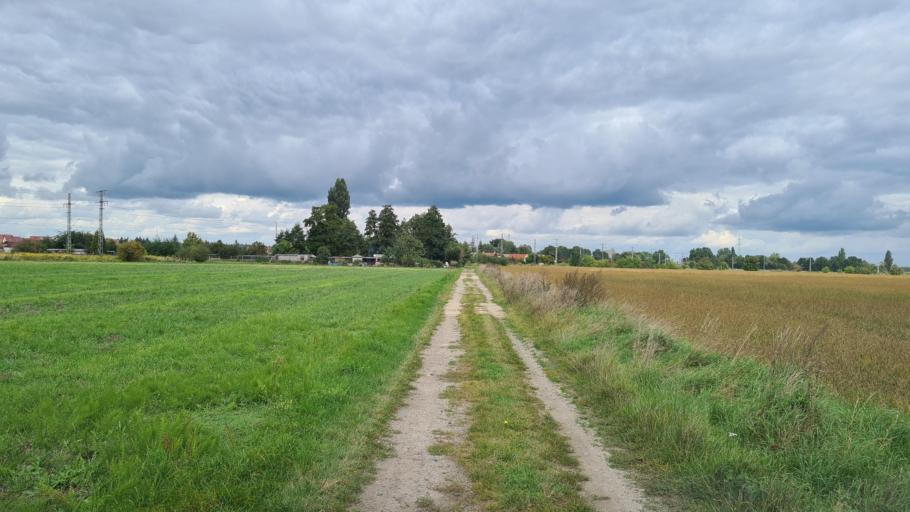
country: DE
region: Brandenburg
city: Doberlug-Kirchhain
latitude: 51.6366
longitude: 13.5741
